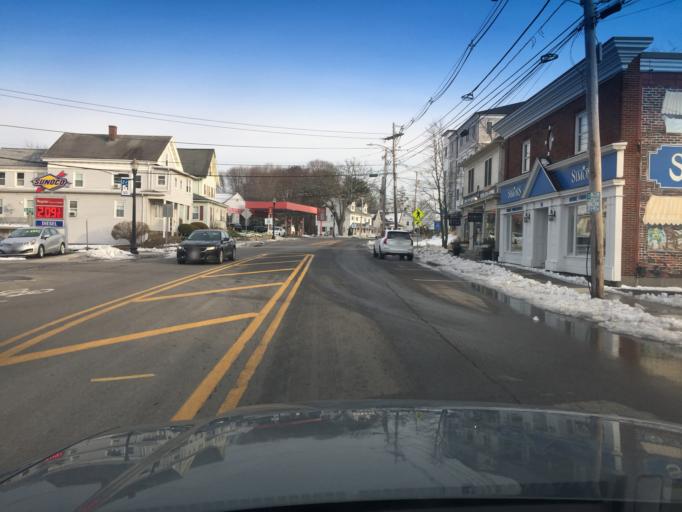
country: US
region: Massachusetts
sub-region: Norfolk County
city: Franklin
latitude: 42.0821
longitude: -71.3951
